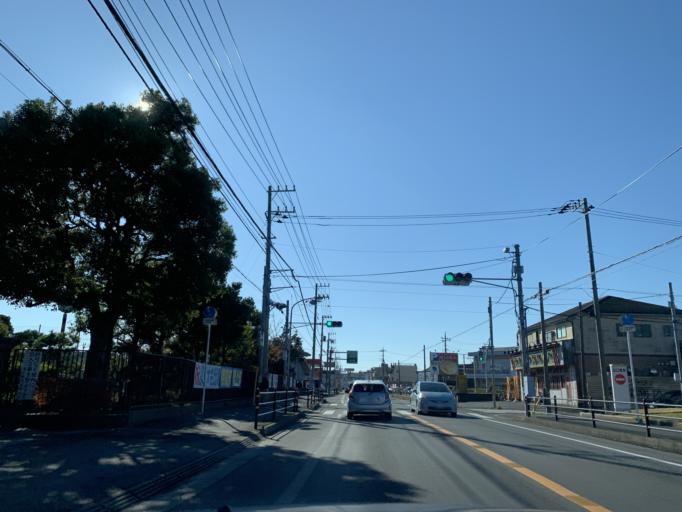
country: JP
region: Chiba
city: Nagareyama
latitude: 35.8484
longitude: 139.8980
